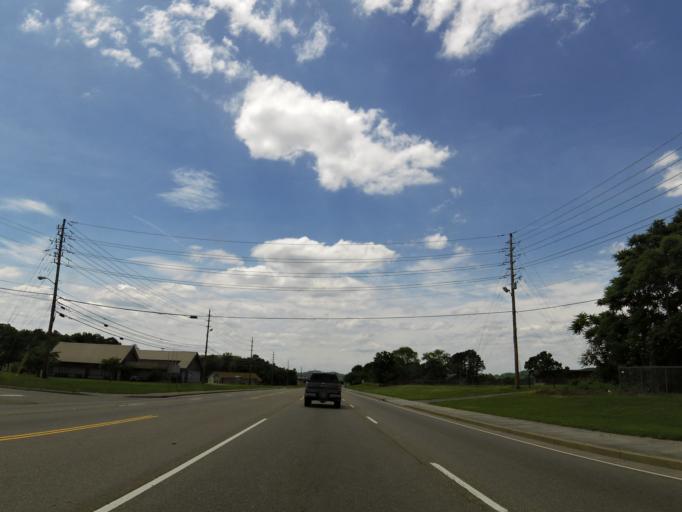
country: US
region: Tennessee
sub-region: Sevier County
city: Sevierville
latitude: 35.8638
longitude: -83.5310
